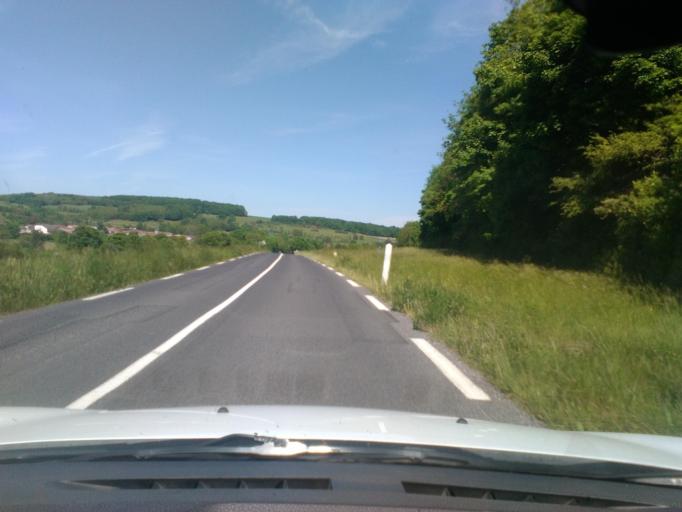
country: FR
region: Lorraine
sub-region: Departement de Meurthe-et-Moselle
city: Gerbeviller
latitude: 48.4578
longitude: 6.5604
